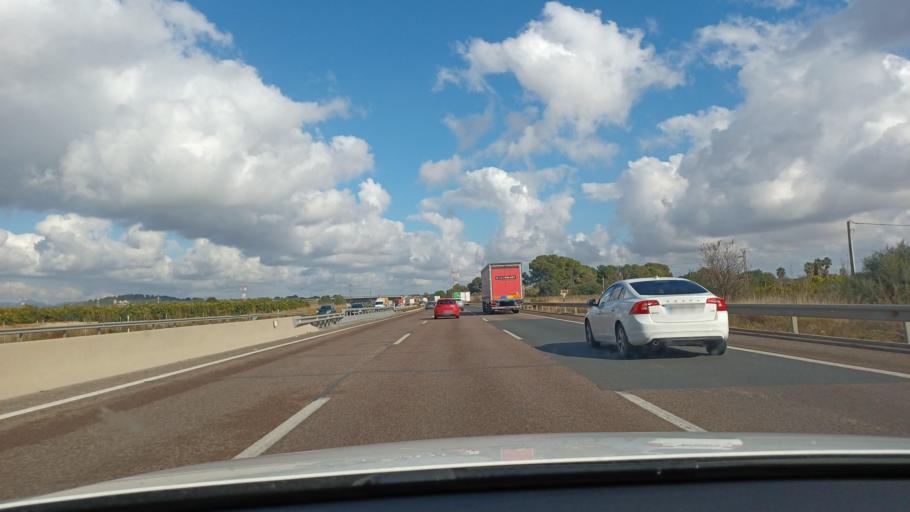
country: ES
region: Valencia
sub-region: Provincia de Valencia
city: Ribarroja
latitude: 39.4931
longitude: -0.5356
